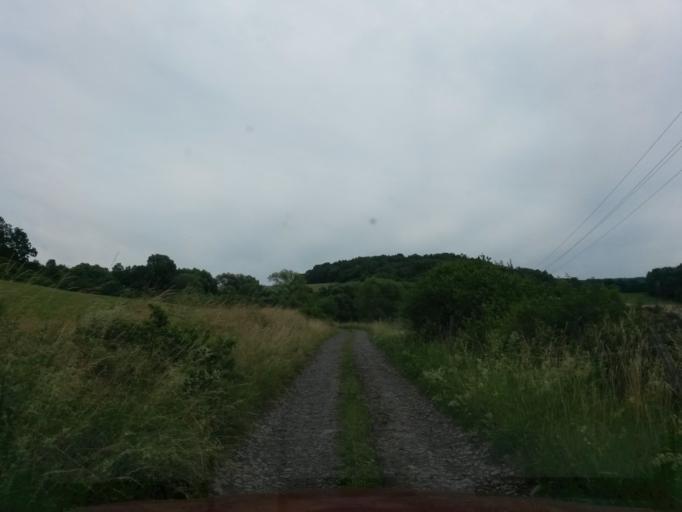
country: SK
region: Banskobystricky
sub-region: Okres Banska Bystrica
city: Zvolen
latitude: 48.4999
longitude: 19.2622
